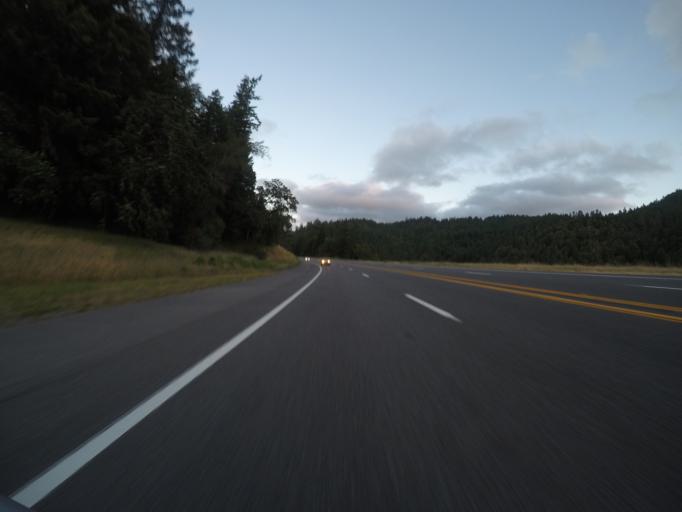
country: US
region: California
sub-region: Humboldt County
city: Redway
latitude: 40.0510
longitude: -123.7922
